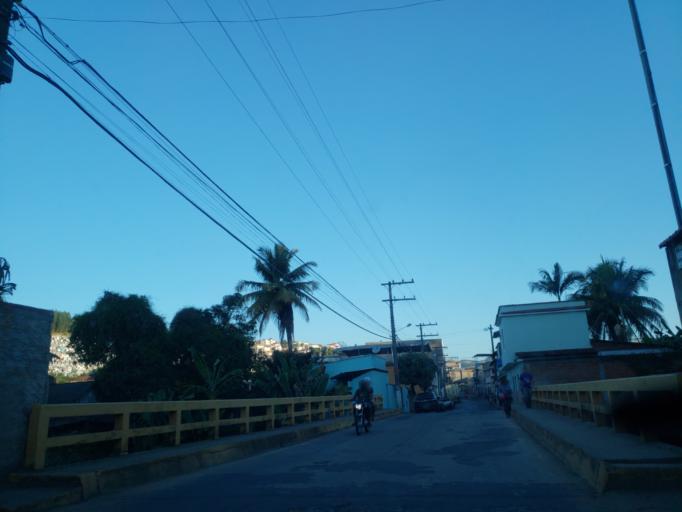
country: BR
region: Minas Gerais
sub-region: Sao Joao Nepomuceno
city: Sao Joao Nepomuceno
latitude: -21.5251
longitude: -43.0149
